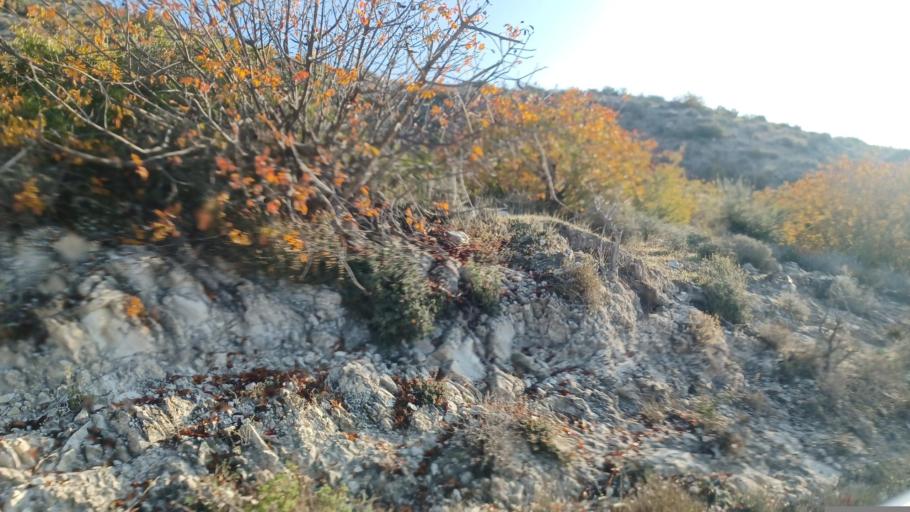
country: CY
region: Larnaka
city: Kofinou
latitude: 34.8232
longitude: 33.3110
